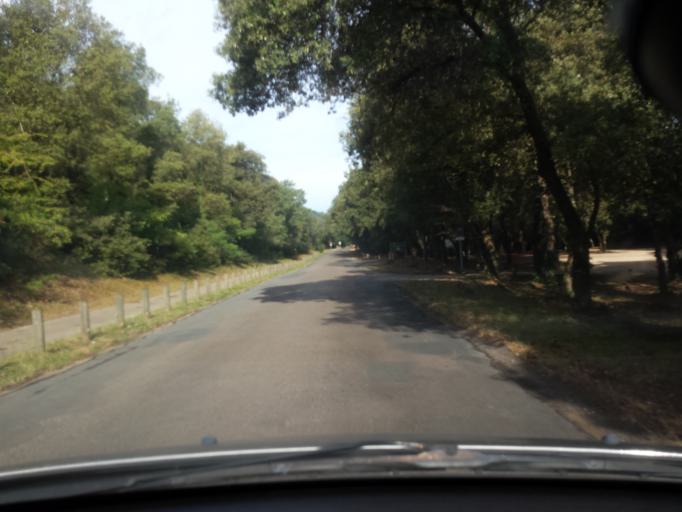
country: FR
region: Pays de la Loire
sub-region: Departement de la Vendee
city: Olonne-sur-Mer
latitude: 46.5449
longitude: -1.8134
